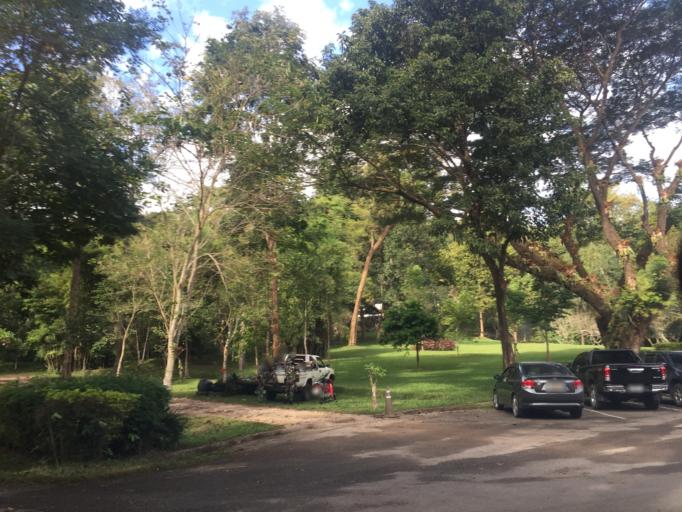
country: TH
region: Lampang
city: Mueang Pan
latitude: 18.8359
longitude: 99.4705
